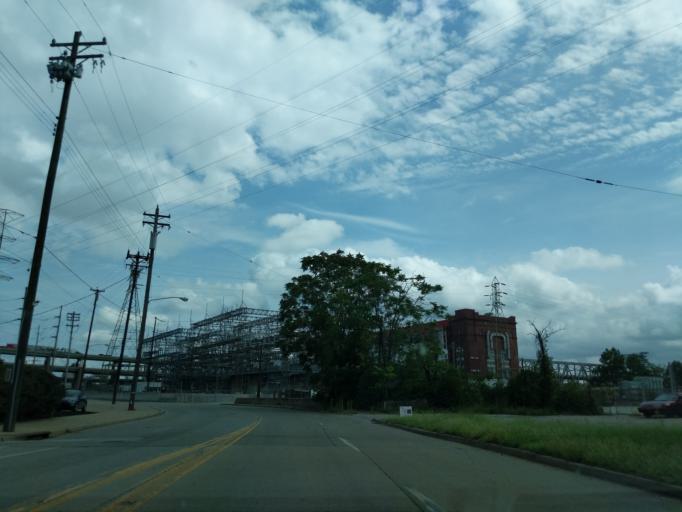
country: US
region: Kentucky
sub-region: Kenton County
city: Covington
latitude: 39.0947
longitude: -84.5263
